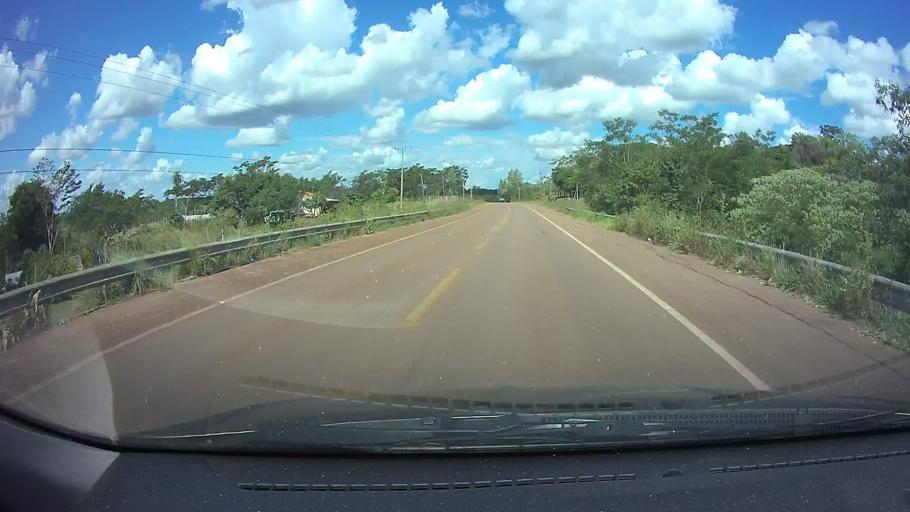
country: PY
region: Paraguari
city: La Colmena
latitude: -25.9164
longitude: -56.7400
